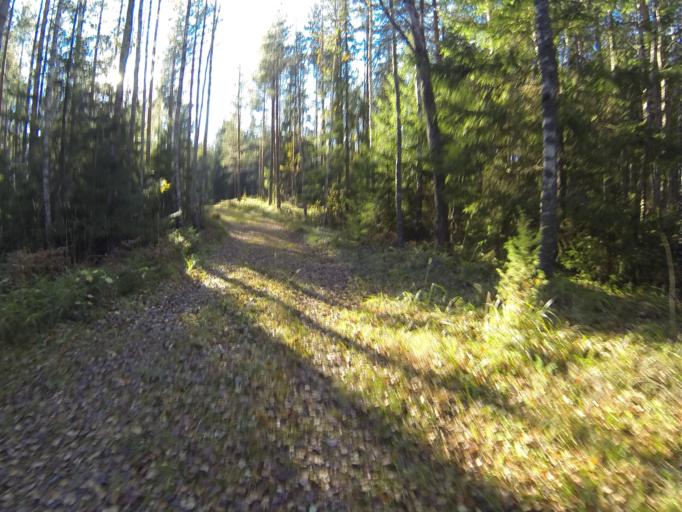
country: FI
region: Varsinais-Suomi
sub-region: Salo
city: Saerkisalo
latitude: 60.2239
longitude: 22.9644
